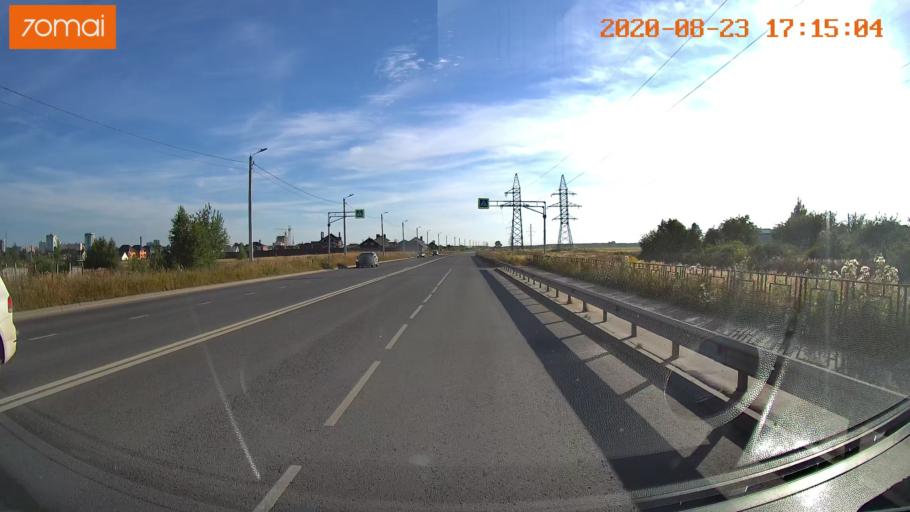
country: RU
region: Ivanovo
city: Novo-Talitsy
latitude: 57.0479
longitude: 40.9170
